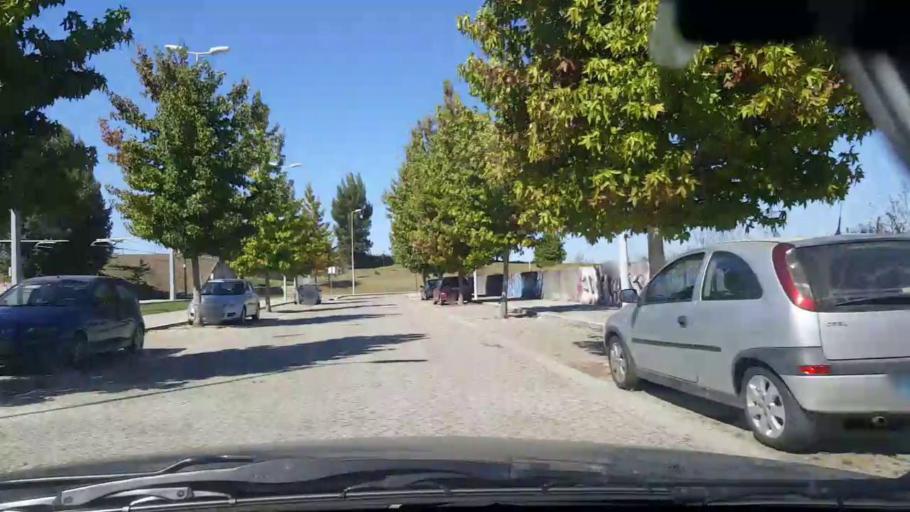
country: PT
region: Porto
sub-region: Matosinhos
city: Lavra
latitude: 41.2851
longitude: -8.6933
